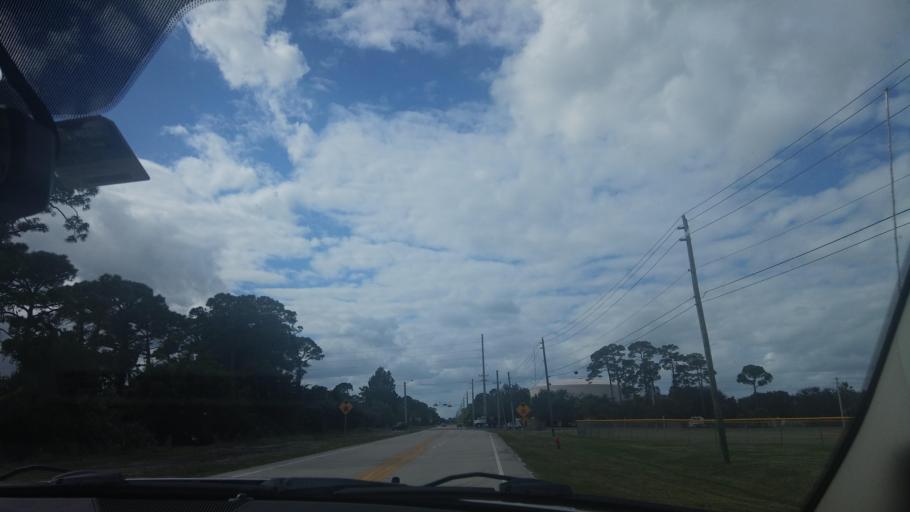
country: US
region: Florida
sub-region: Indian River County
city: Winter Beach
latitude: 27.7338
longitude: -80.4440
